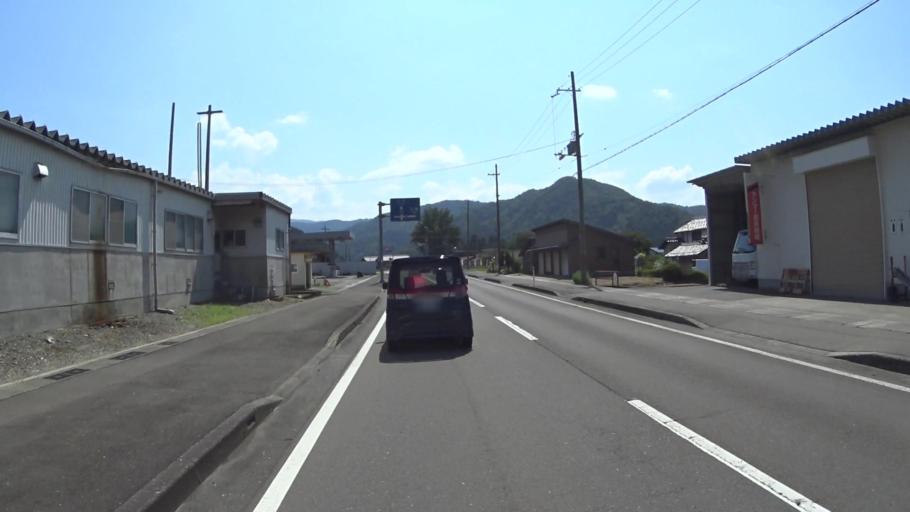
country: JP
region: Fukui
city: Obama
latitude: 35.4262
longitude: 135.6898
